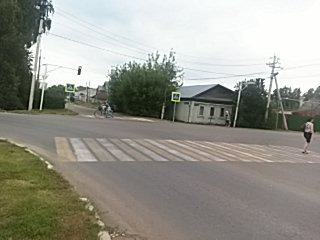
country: RU
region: Tatarstan
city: Yelabuga
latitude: 55.7550
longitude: 52.0818
